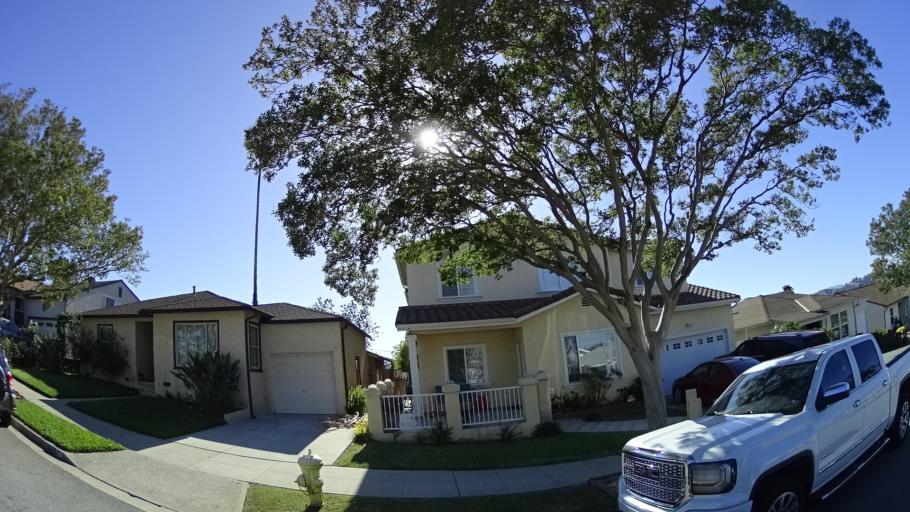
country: US
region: California
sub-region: Los Angeles County
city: Alhambra
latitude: 34.0753
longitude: -118.1548
